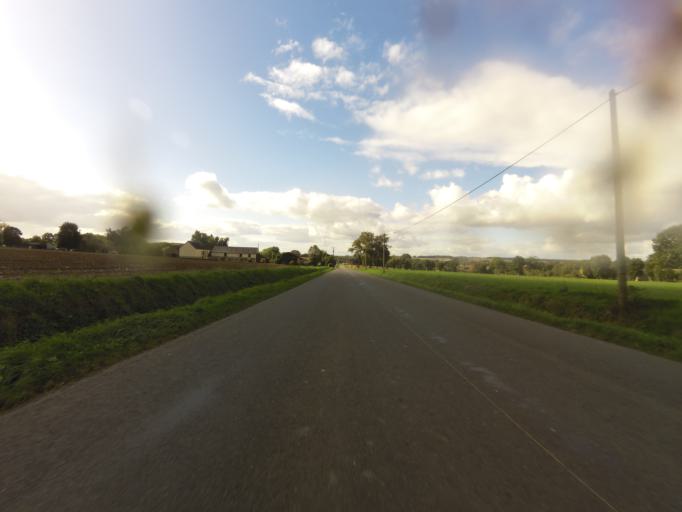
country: FR
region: Brittany
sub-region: Departement d'Ille-et-Vilaine
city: Chasne-sur-Illet
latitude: 48.2557
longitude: -1.5452
